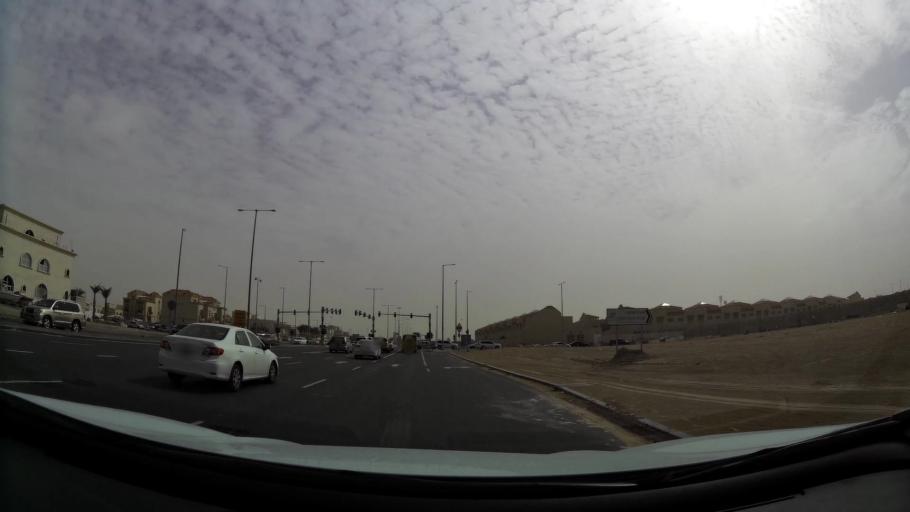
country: AE
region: Abu Dhabi
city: Abu Dhabi
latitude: 24.4044
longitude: 54.5717
